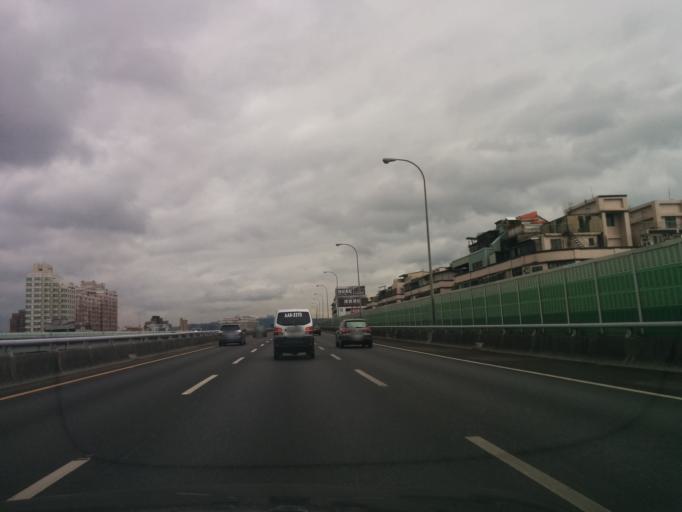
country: TW
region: Taipei
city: Taipei
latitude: 25.0762
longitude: 121.4942
